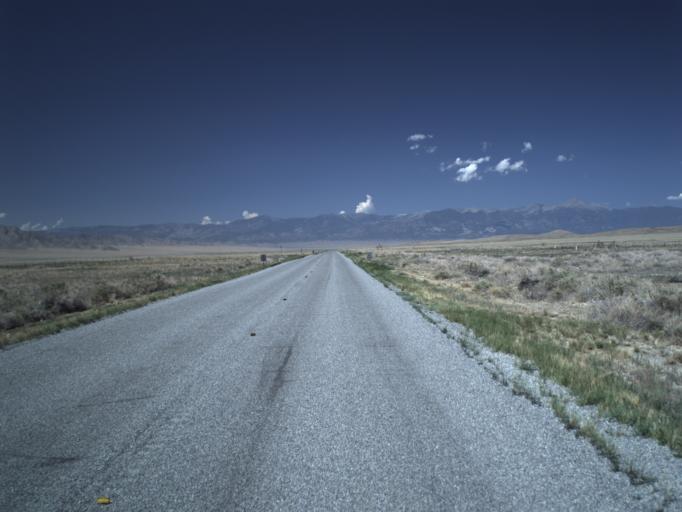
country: US
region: Utah
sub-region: Beaver County
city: Milford
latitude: 39.0609
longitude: -113.7549
